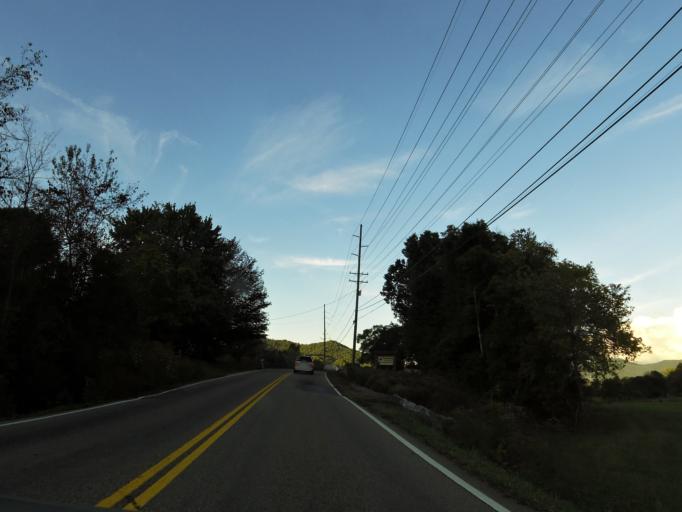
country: US
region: Tennessee
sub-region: Sevier County
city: Pigeon Forge
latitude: 35.7074
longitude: -83.6696
